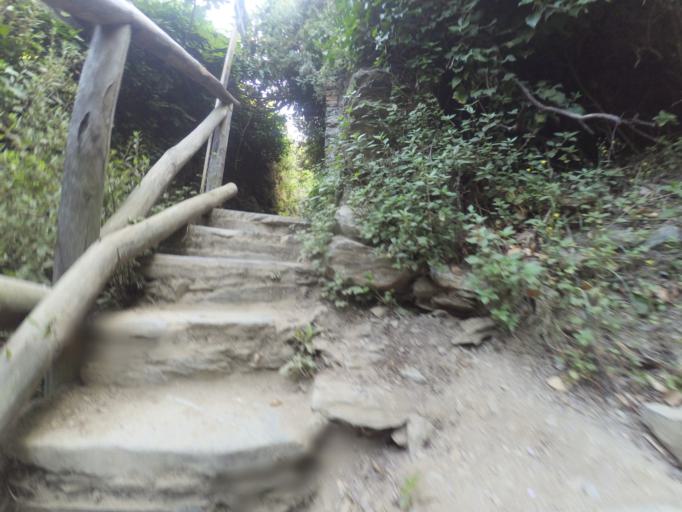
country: IT
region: Liguria
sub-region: Provincia di La Spezia
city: Monterosso al Mare
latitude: 44.1454
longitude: 9.6615
